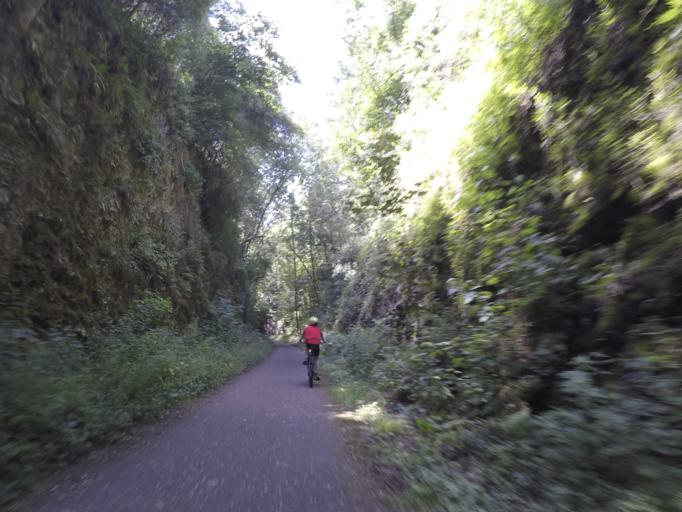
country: BE
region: Wallonia
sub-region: Province de Liege
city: Modave
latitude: 50.4442
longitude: 5.3188
